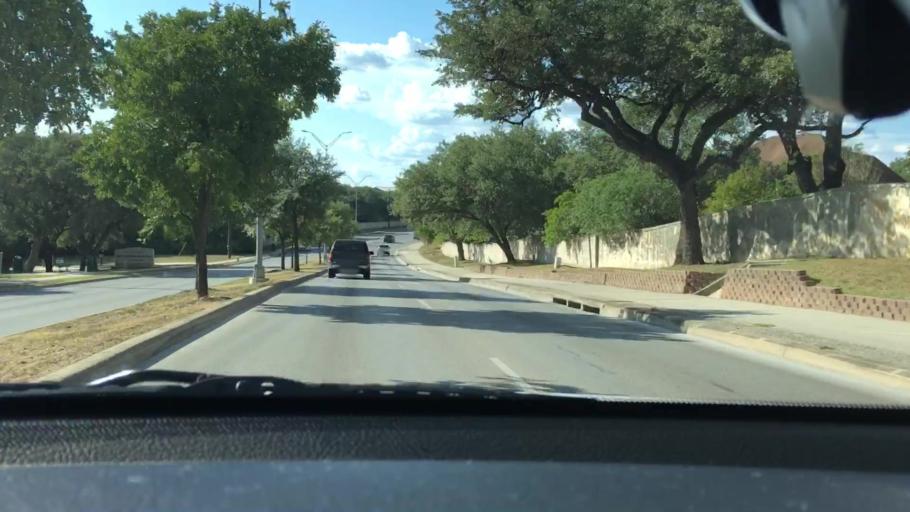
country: US
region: Texas
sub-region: Guadalupe County
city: Schertz
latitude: 29.5768
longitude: -98.2796
